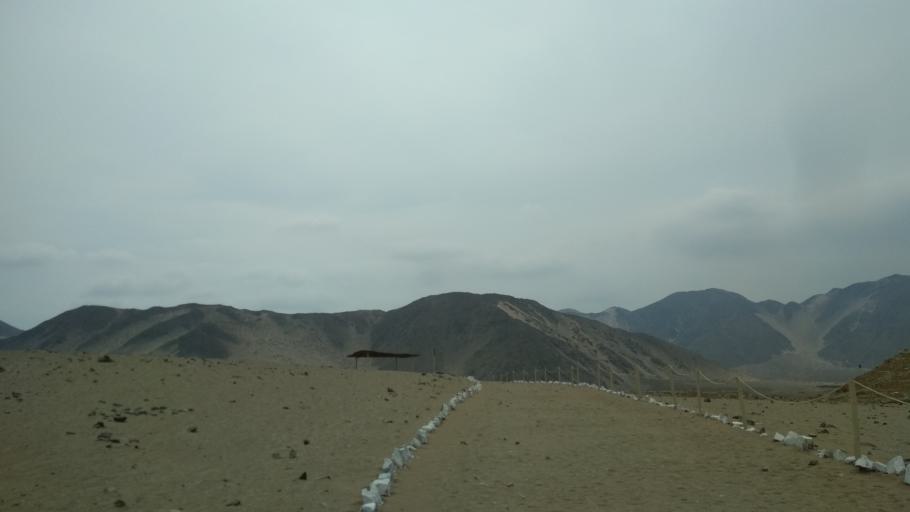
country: PE
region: Lima
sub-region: Huaura
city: Vegueta
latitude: -10.8936
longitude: -77.5180
